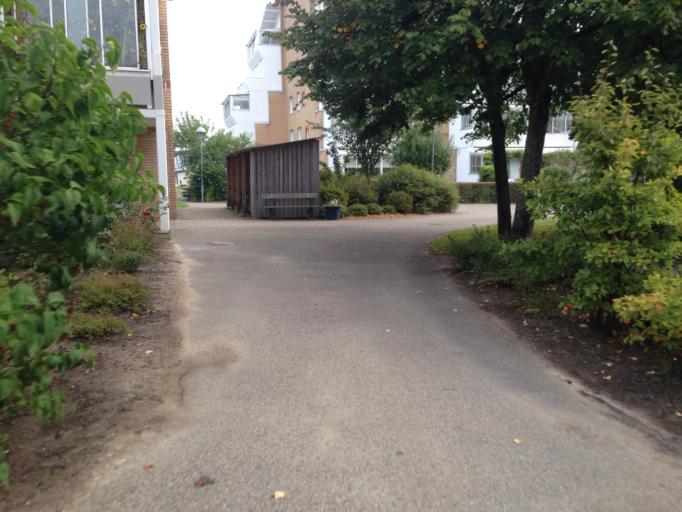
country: SE
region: Skane
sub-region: Lomma Kommun
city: Lomma
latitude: 55.6742
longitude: 13.0653
